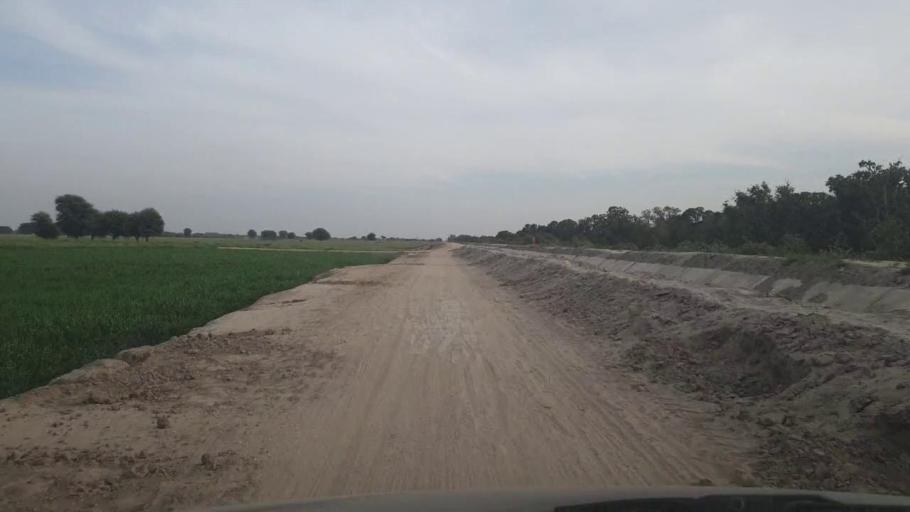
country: PK
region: Sindh
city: Kunri
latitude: 25.2713
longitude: 69.5620
